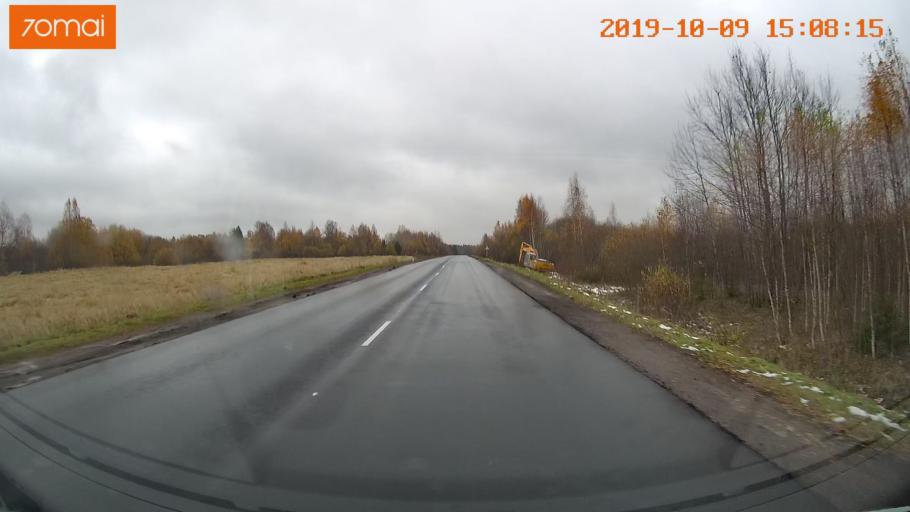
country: RU
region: Kostroma
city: Susanino
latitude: 58.2087
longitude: 41.6486
